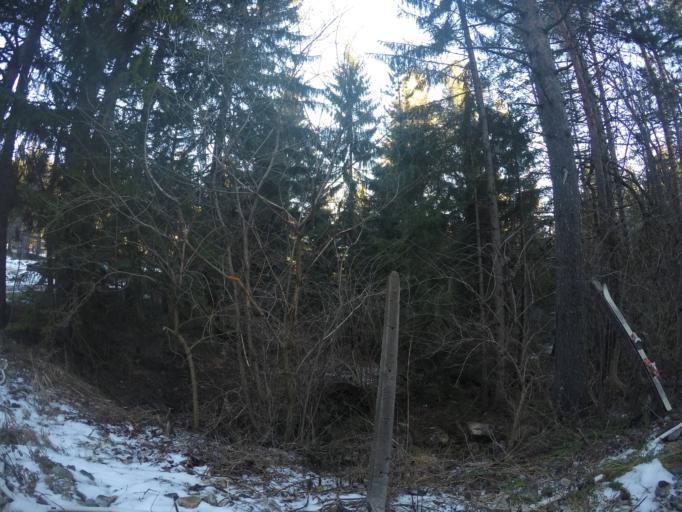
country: BG
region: Blagoevgrad
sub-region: Obshtina Bansko
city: Bansko
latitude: 41.8103
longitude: 23.4648
